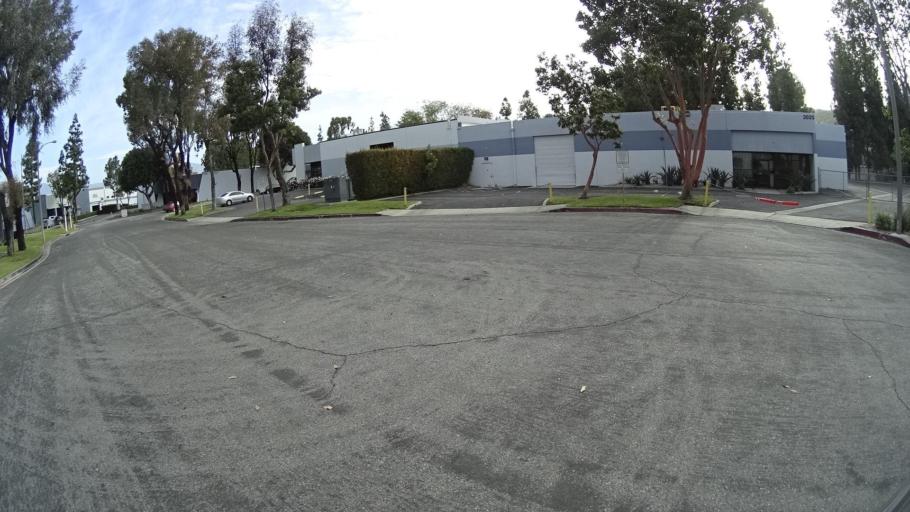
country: US
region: California
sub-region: Los Angeles County
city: South El Monte
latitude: 34.0245
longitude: -118.0389
